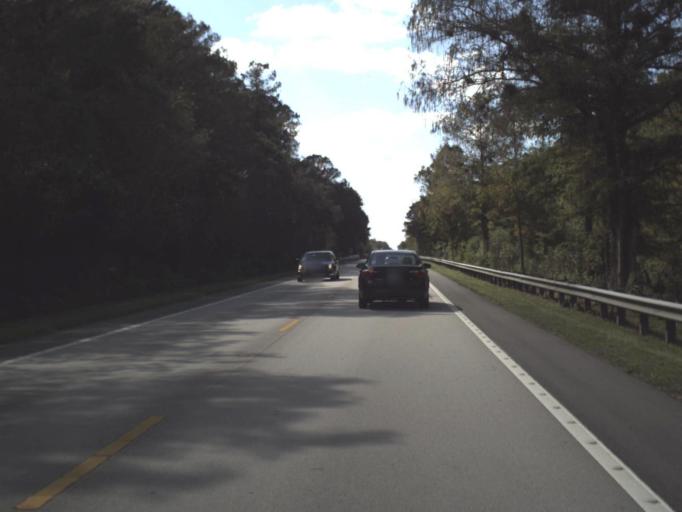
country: US
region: Florida
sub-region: Miami-Dade County
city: Kendall West
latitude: 25.8594
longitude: -81.0580
